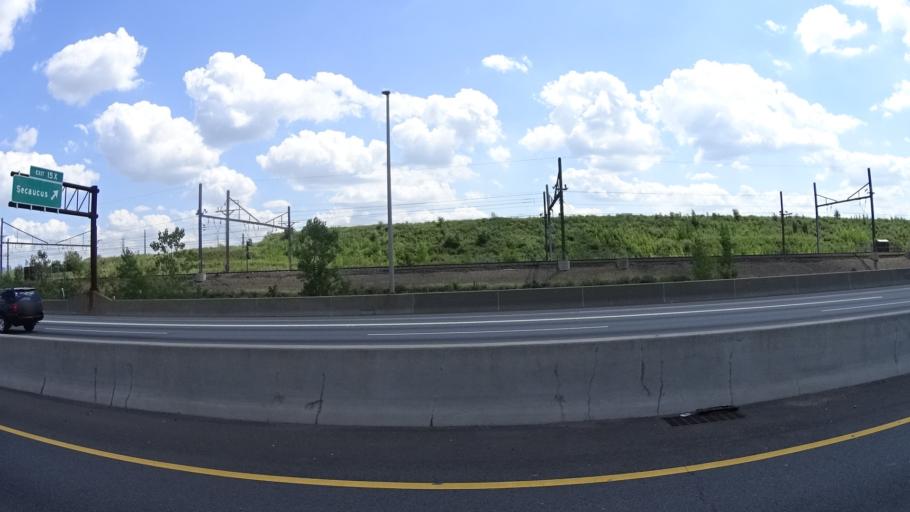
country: US
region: New Jersey
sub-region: Hudson County
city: Jersey City
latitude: 40.7601
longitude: -74.0805
